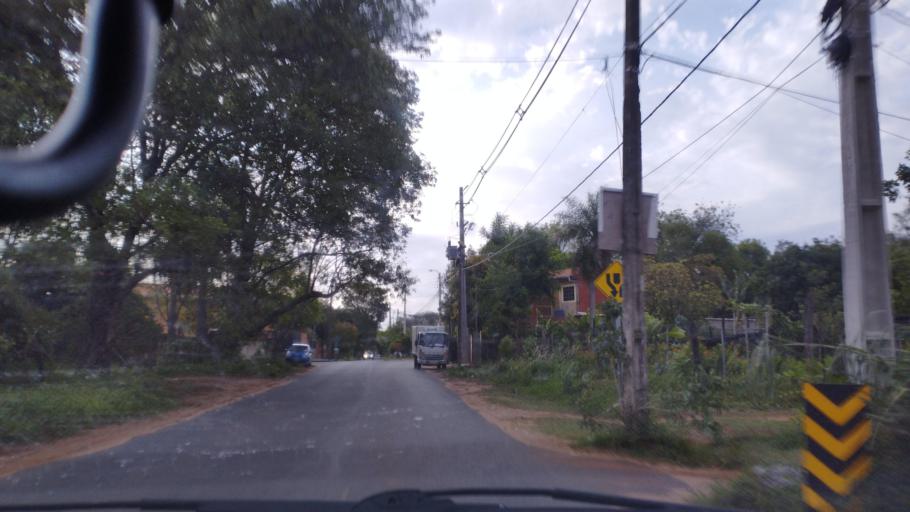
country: PY
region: Central
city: Fernando de la Mora
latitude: -25.3030
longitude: -57.5178
